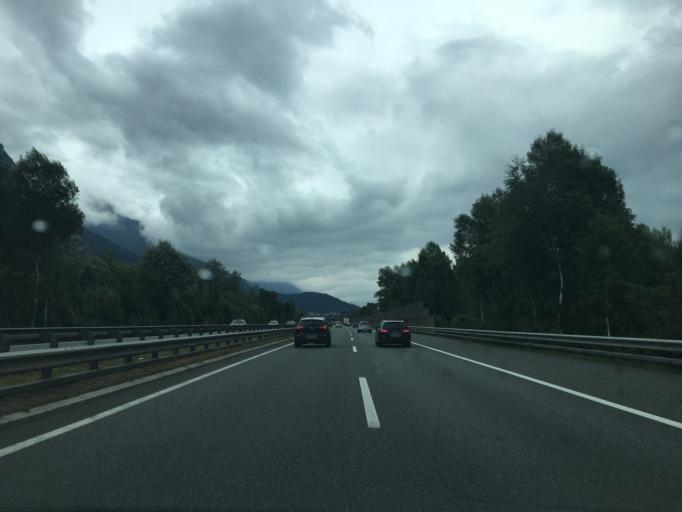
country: AT
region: Tyrol
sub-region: Politischer Bezirk Schwaz
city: Buch bei Jenbach
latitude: 47.3725
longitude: 11.7405
